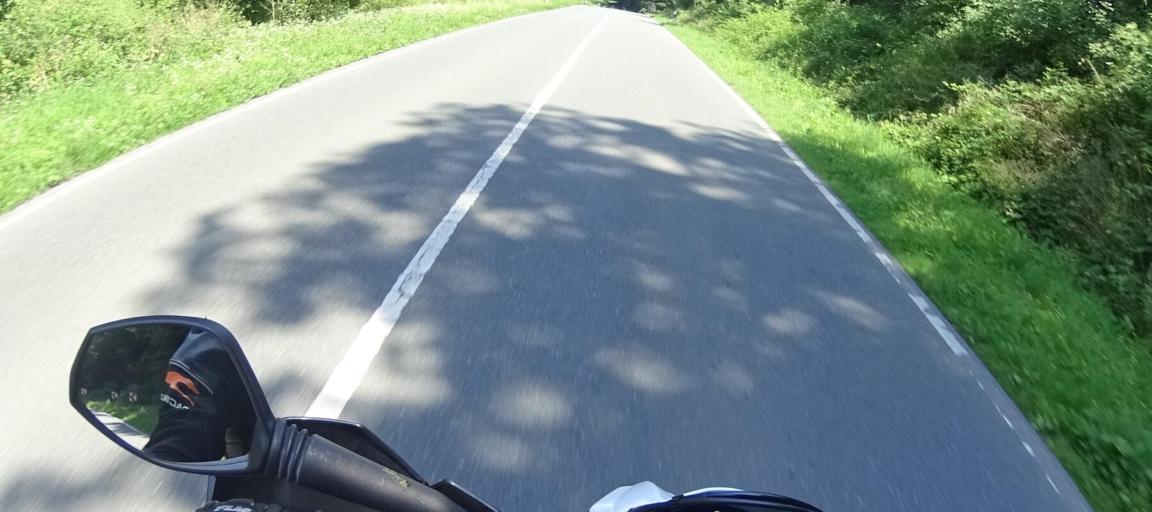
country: DE
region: North Rhine-Westphalia
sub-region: Regierungsbezirk Detmold
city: Hoexter
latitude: 51.7699
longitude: 9.4168
